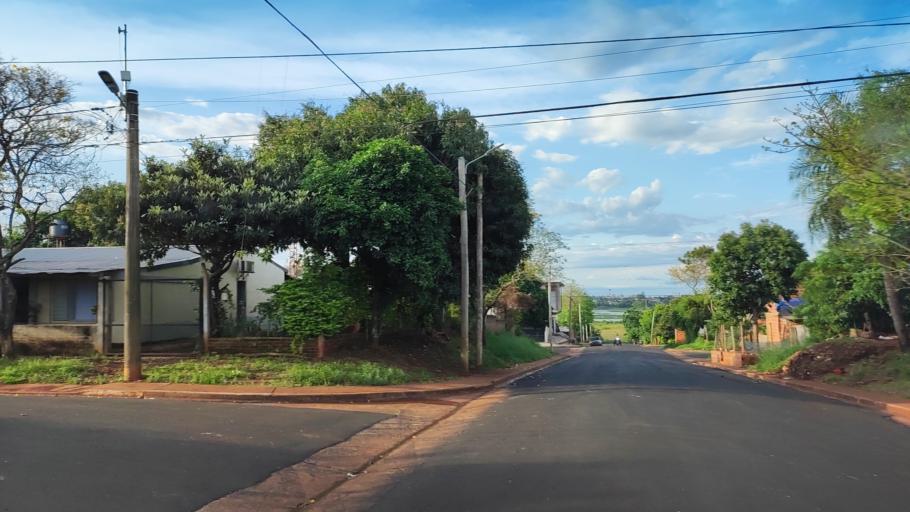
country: AR
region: Misiones
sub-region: Departamento de Capital
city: Posadas
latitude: -27.4347
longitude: -55.9071
